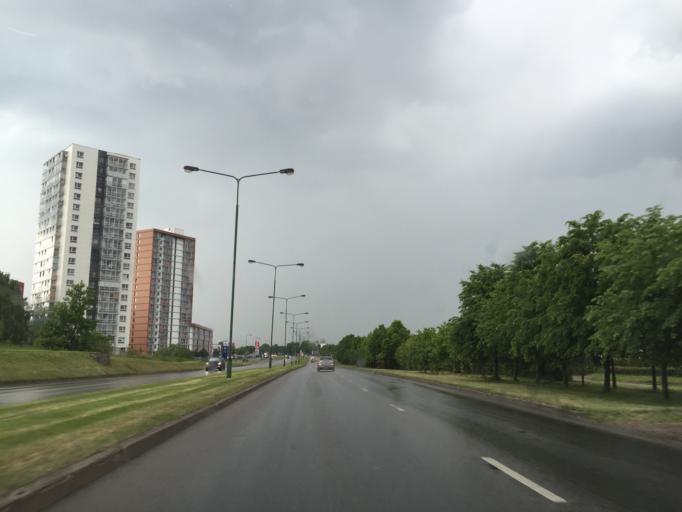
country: LT
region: Klaipedos apskritis
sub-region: Klaipeda
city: Klaipeda
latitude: 55.7475
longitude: 21.1308
